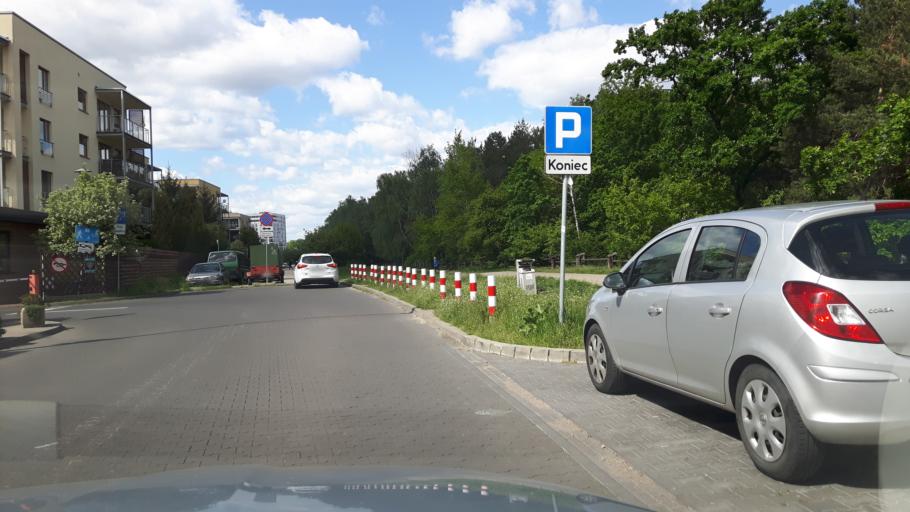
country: PL
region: Masovian Voivodeship
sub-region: Warszawa
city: Targowek
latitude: 52.2935
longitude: 21.0574
